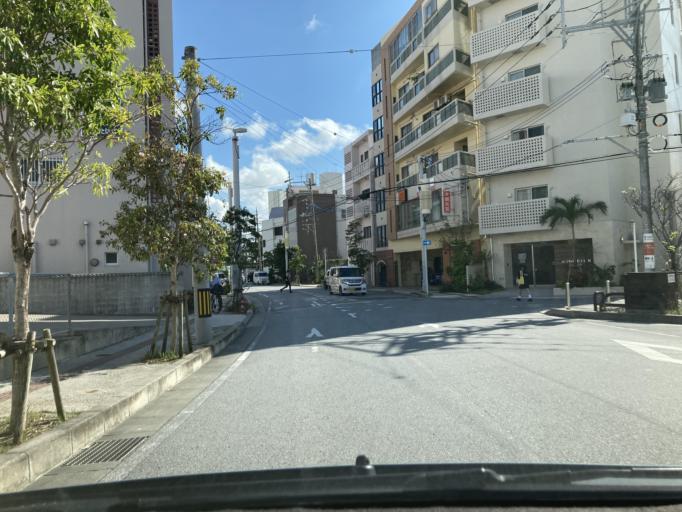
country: JP
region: Okinawa
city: Naha-shi
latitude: 26.2135
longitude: 127.6903
